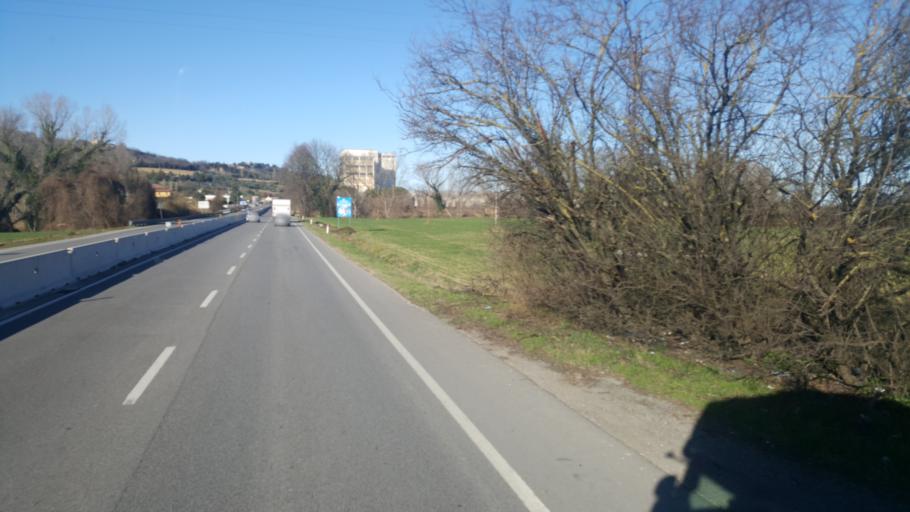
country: IT
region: Emilia-Romagna
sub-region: Provincia di Rimini
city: Cerasolo
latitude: 44.0141
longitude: 12.5467
